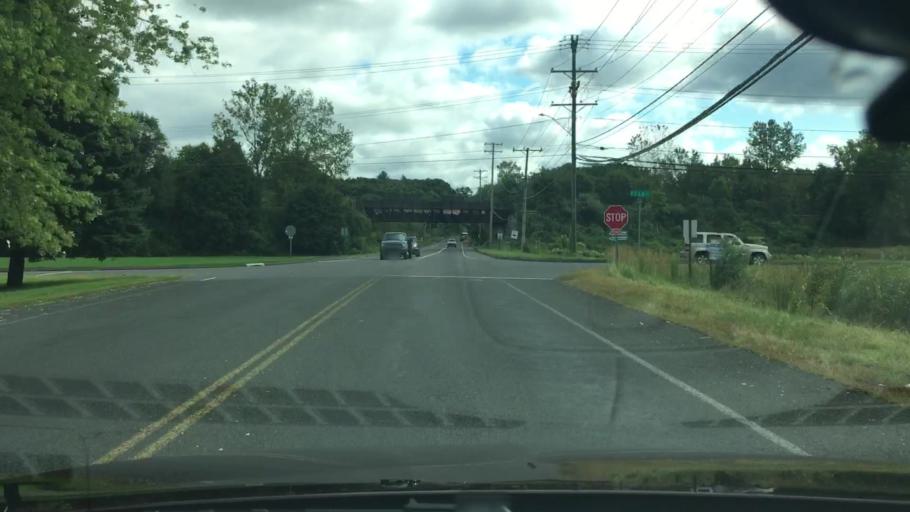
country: US
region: Connecticut
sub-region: New Haven County
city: Cheshire Village
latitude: 41.5557
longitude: -72.9040
